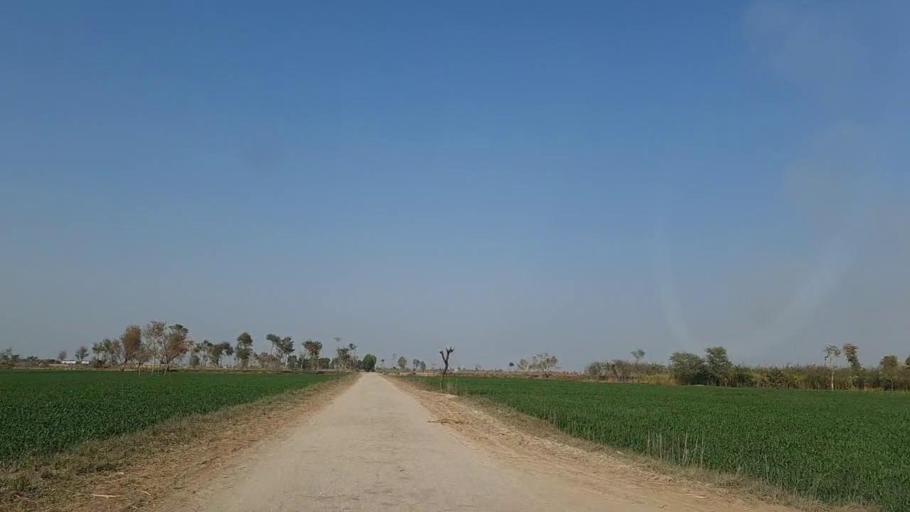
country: PK
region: Sindh
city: Daur
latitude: 26.4665
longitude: 68.3046
